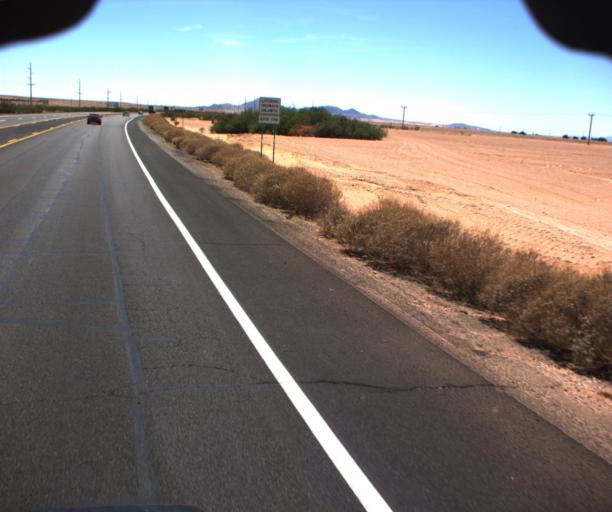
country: US
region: Arizona
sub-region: La Paz County
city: Parker
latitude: 34.1352
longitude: -114.2805
